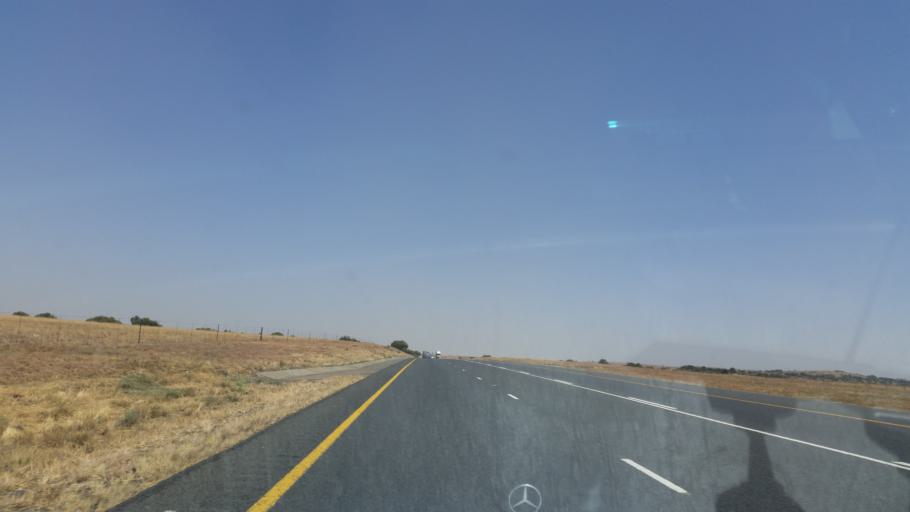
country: ZA
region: Orange Free State
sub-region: Lejweleputswa District Municipality
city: Winburg
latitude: -28.6996
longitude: 26.8008
